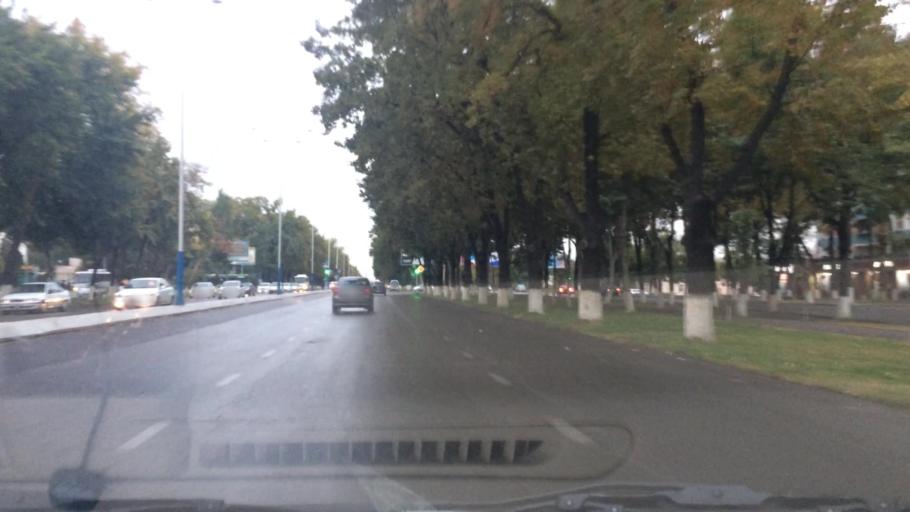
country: UZ
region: Toshkent Shahri
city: Tashkent
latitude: 41.2698
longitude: 69.2019
